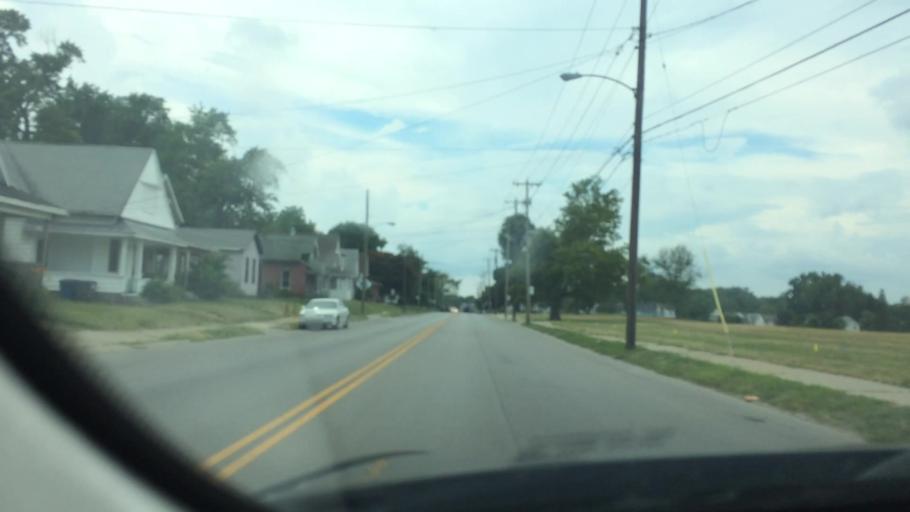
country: US
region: Ohio
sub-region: Wood County
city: Rossford
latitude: 41.6347
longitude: -83.5689
